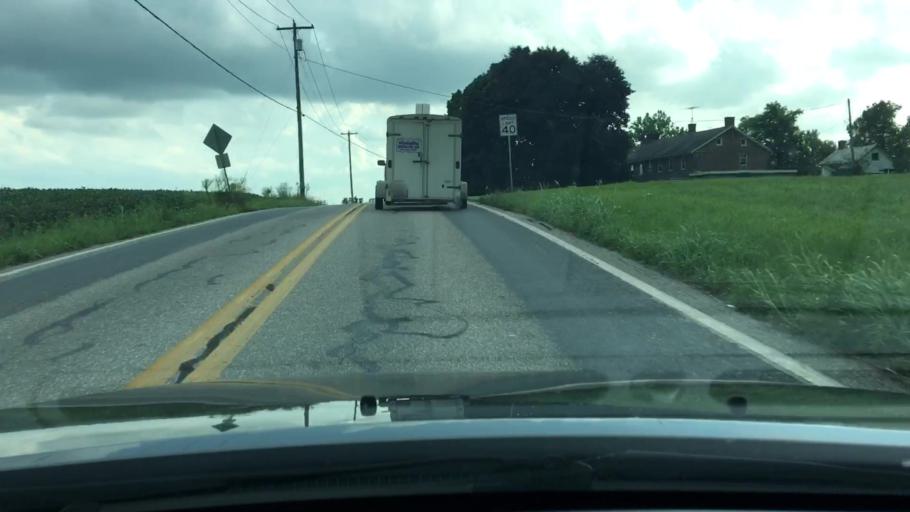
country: US
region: Pennsylvania
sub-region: Franklin County
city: Scotland
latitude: 39.9615
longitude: -77.5834
